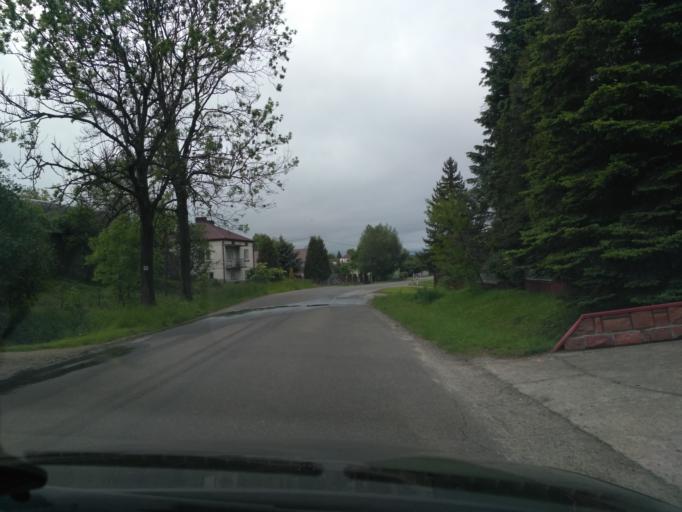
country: PL
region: Subcarpathian Voivodeship
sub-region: Powiat jasielski
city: Brzyska
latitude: 49.8062
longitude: 21.4029
